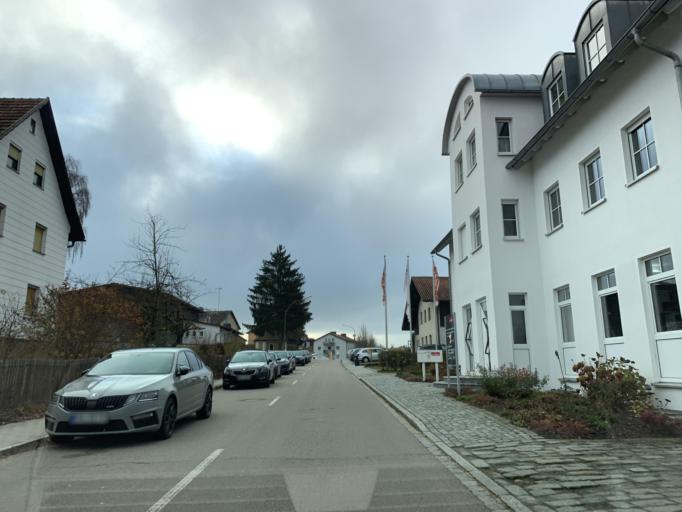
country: DE
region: Bavaria
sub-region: Upper Palatinate
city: Roetz
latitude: 49.3450
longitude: 12.5304
